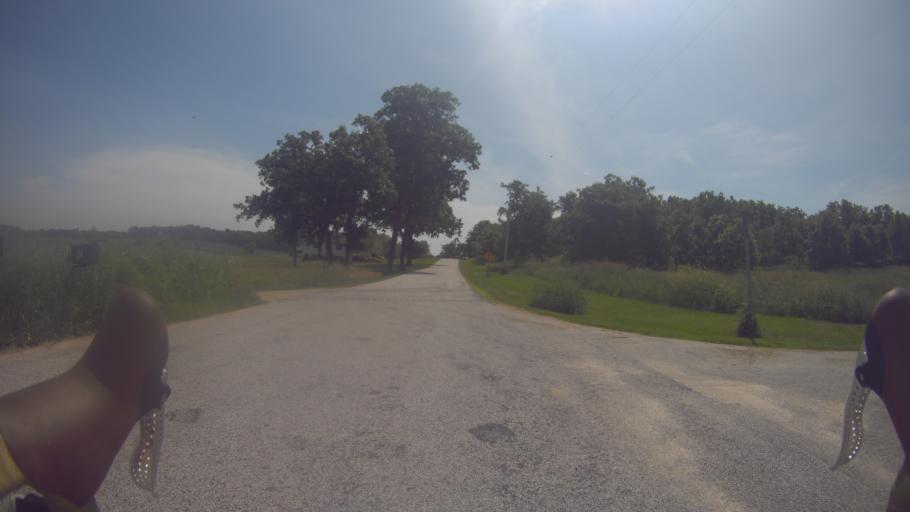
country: US
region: Wisconsin
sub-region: Dane County
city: Deerfield
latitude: 43.0565
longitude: -89.0313
